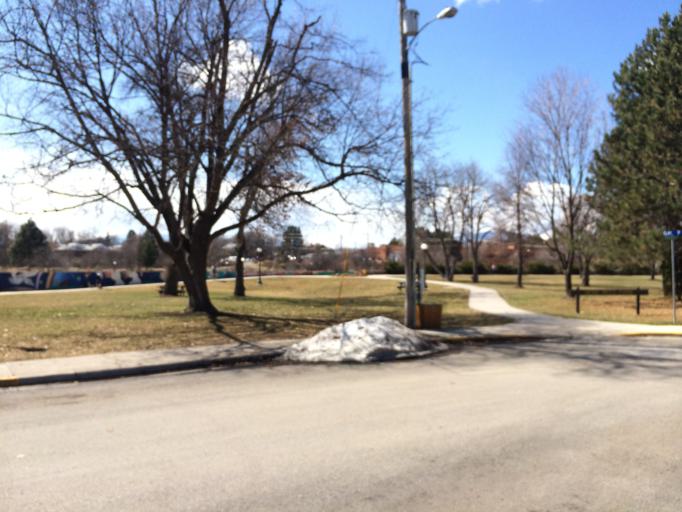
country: US
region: Montana
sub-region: Missoula County
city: Missoula
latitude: 46.8677
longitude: -113.9929
